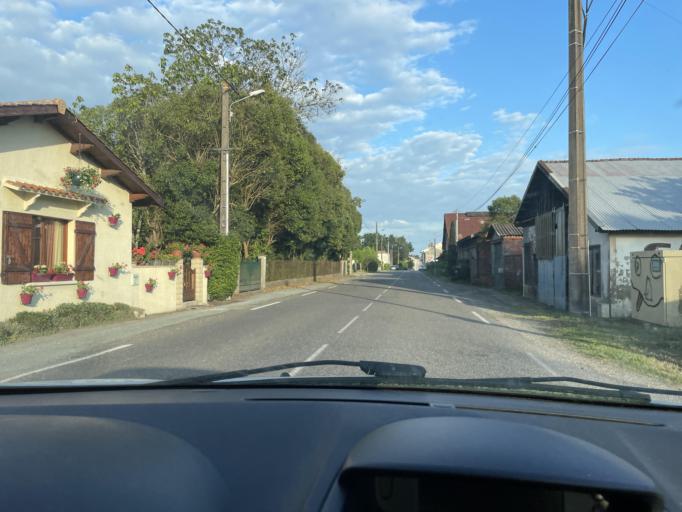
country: FR
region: Aquitaine
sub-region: Departement de la Gironde
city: Grignols
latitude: 44.3896
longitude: -0.0483
